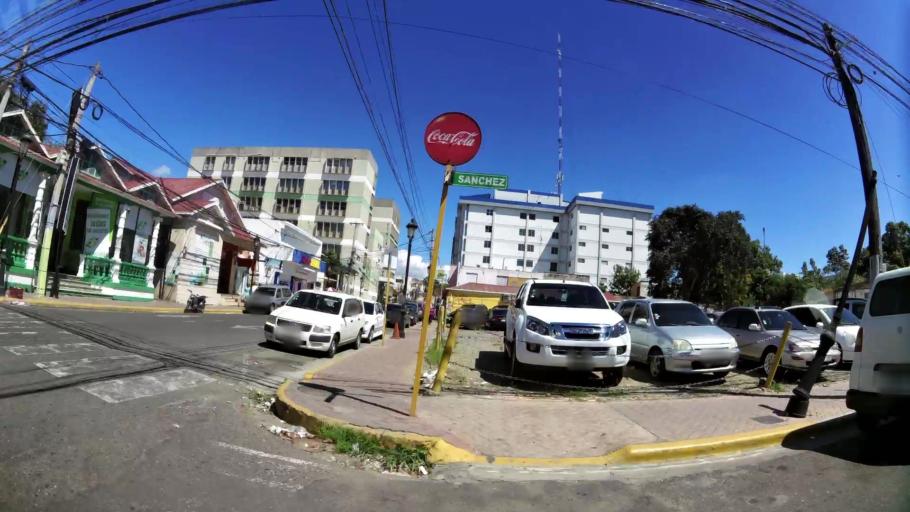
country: DO
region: Santiago
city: Santiago de los Caballeros
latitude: 19.4522
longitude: -70.7010
